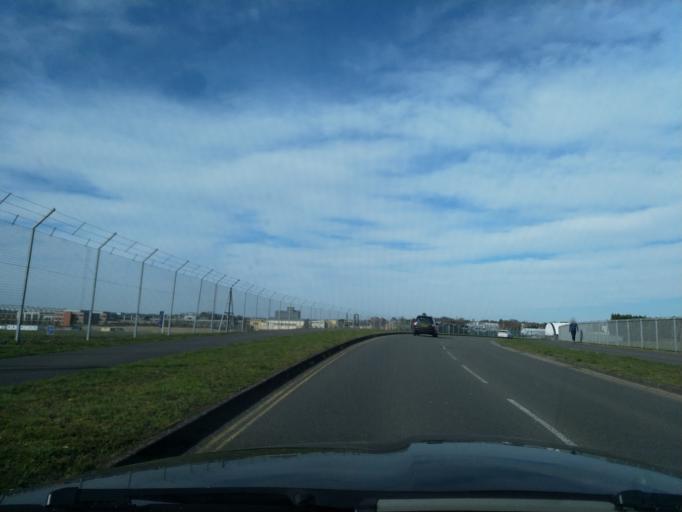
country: GB
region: England
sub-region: Hampshire
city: Farnborough
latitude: 51.2792
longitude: -0.7560
